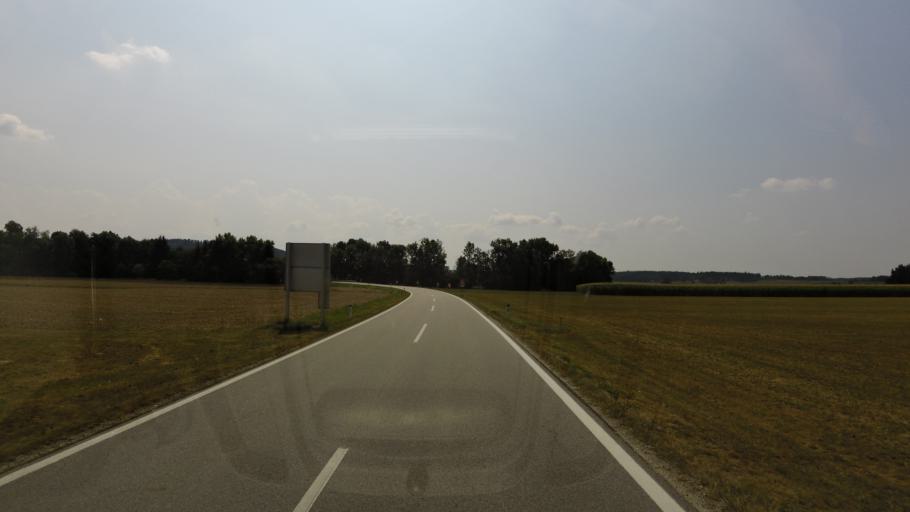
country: DE
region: Bavaria
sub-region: Lower Bavaria
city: Bad Fussing
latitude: 48.2661
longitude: 13.3303
